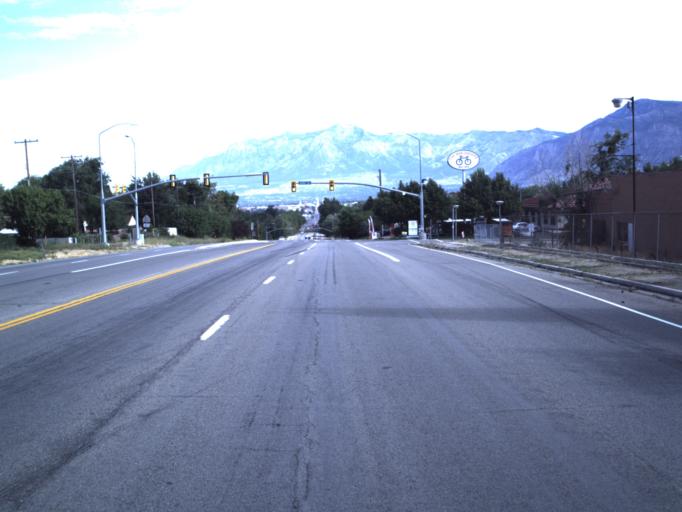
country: US
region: Utah
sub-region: Weber County
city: Washington Terrace
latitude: 41.1805
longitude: -111.9713
